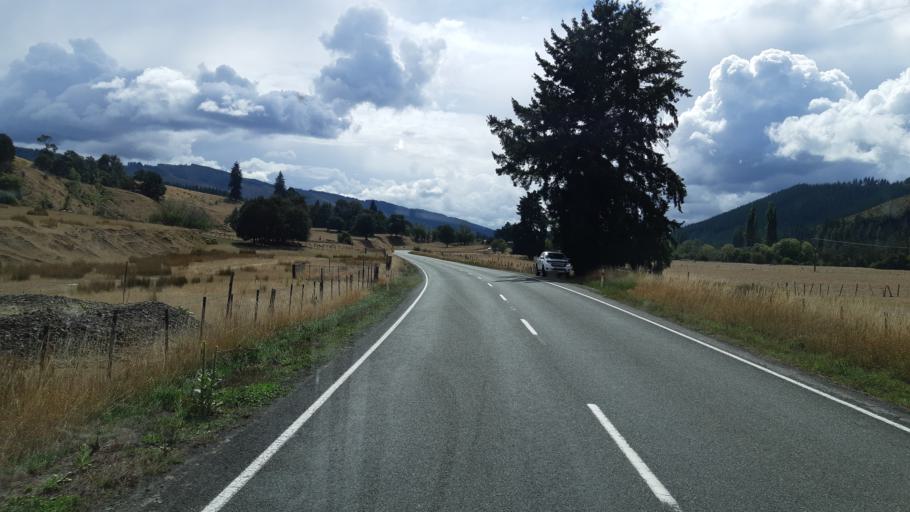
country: NZ
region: Tasman
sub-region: Tasman District
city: Wakefield
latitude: -41.4858
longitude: 172.7990
